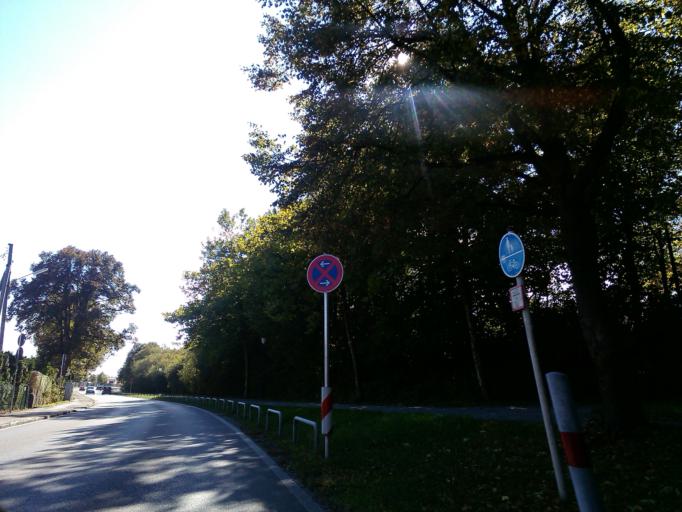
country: DE
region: Bavaria
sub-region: Upper Bavaria
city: Starnberg
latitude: 48.0157
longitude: 11.3495
